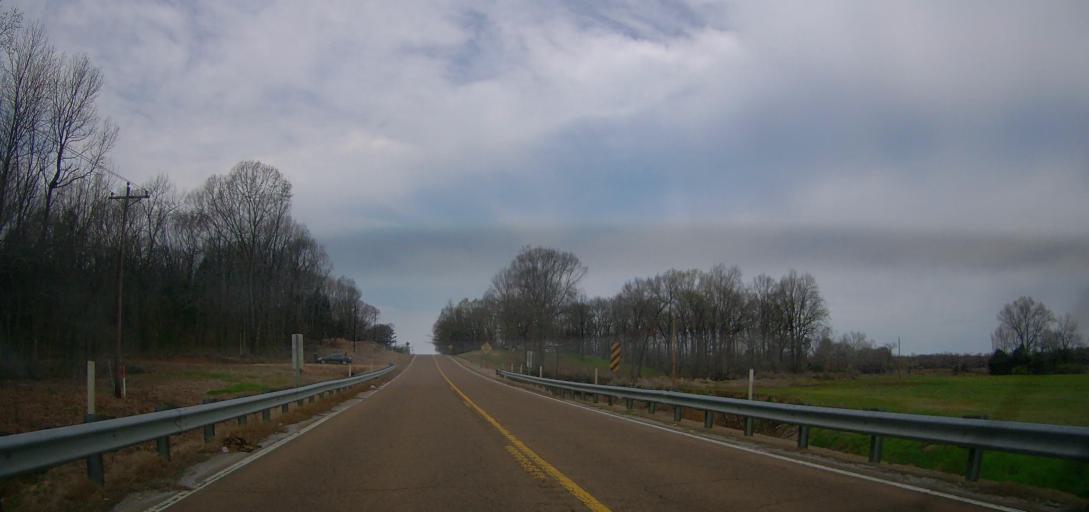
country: US
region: Mississippi
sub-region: Marshall County
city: Byhalia
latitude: 34.8581
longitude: -89.6485
